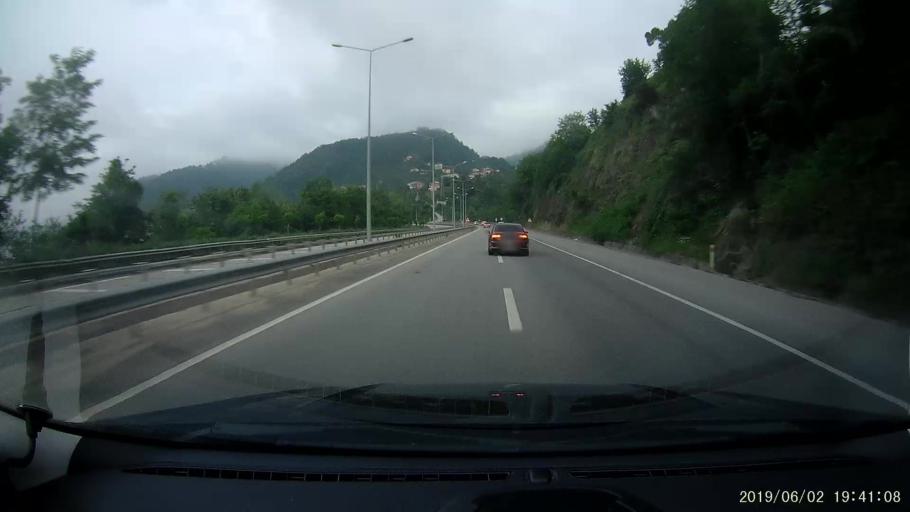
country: TR
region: Giresun
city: Kesap
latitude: 40.9164
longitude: 38.4744
